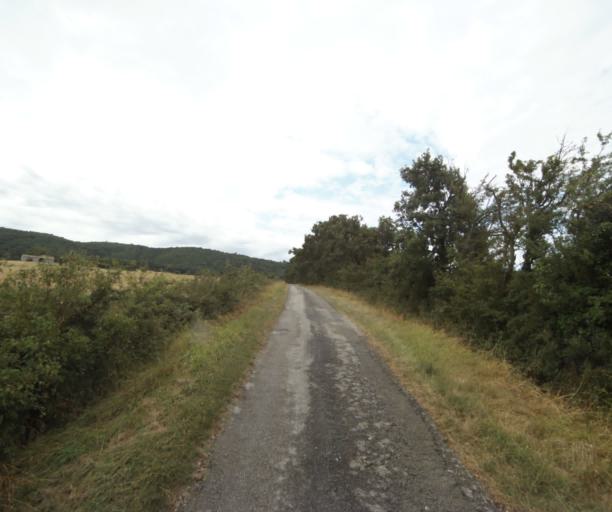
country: FR
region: Midi-Pyrenees
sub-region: Departement de la Haute-Garonne
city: Revel
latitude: 43.4208
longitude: 1.9774
